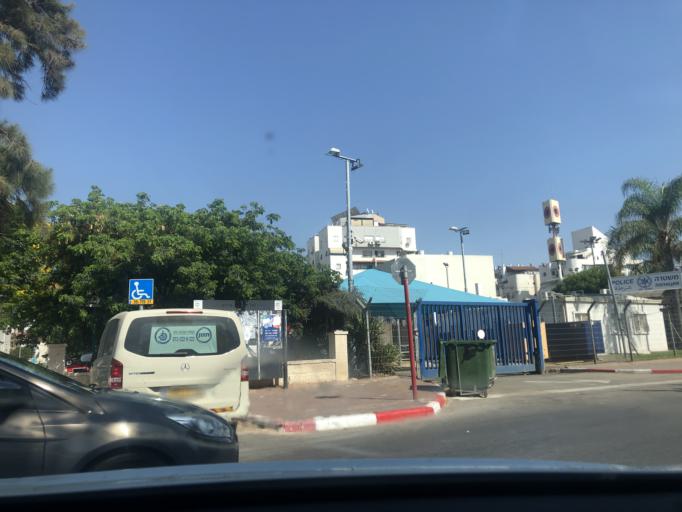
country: IL
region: Central District
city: Lod
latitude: 31.9520
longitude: 34.8936
